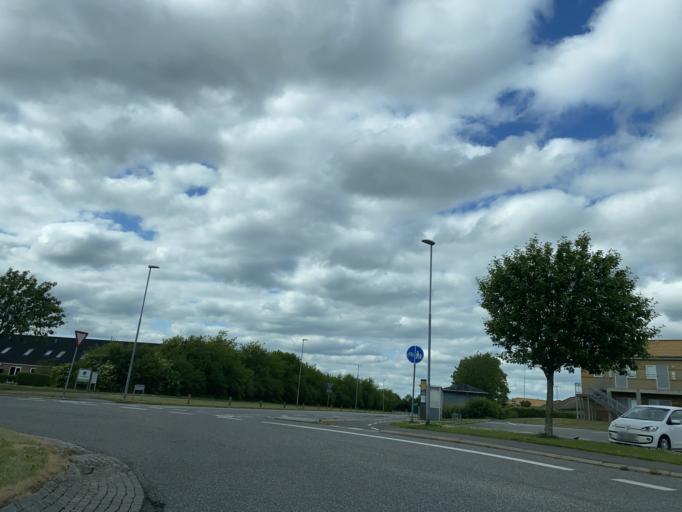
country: DK
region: Central Jutland
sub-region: Arhus Kommune
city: Framlev
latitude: 56.1438
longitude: 9.9878
